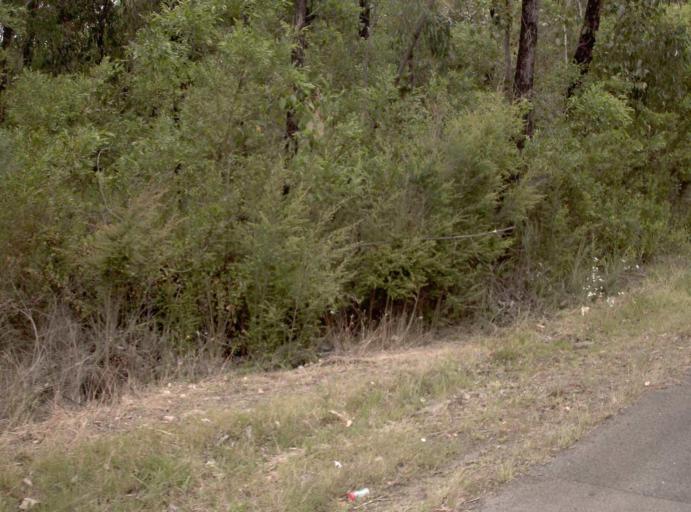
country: AU
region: Victoria
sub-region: Latrobe
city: Moe
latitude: -38.3197
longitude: 146.2604
